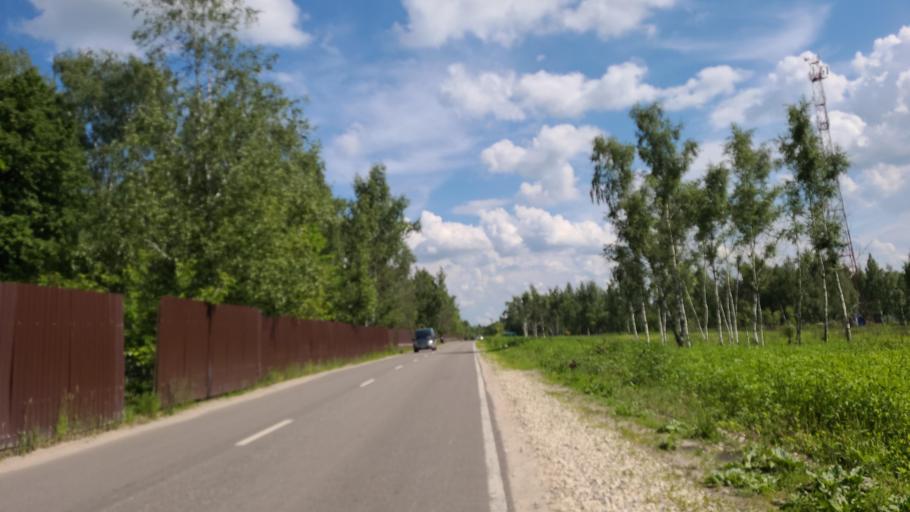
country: RU
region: Moskovskaya
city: Konobeyevo
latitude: 55.4006
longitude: 38.6771
